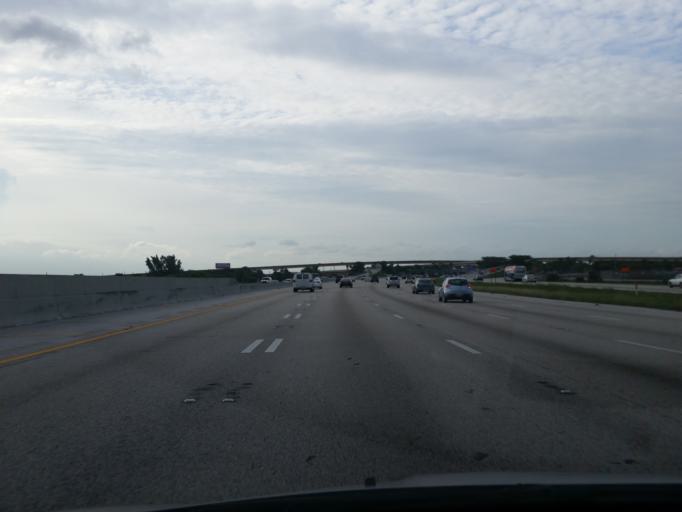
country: US
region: Florida
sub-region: Broward County
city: Dania Beach
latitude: 26.0746
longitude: -80.1677
